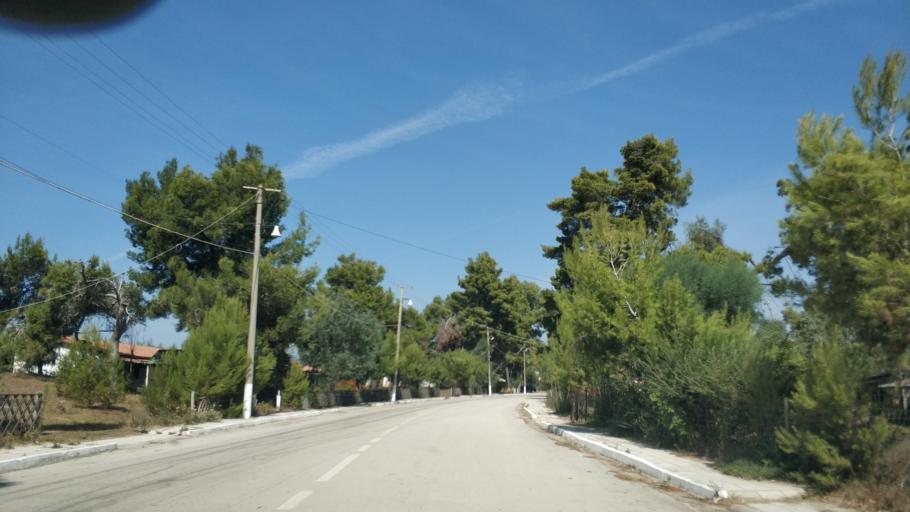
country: AL
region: Fier
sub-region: Rrethi i Lushnjes
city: Divjake
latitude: 40.9679
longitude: 19.4786
